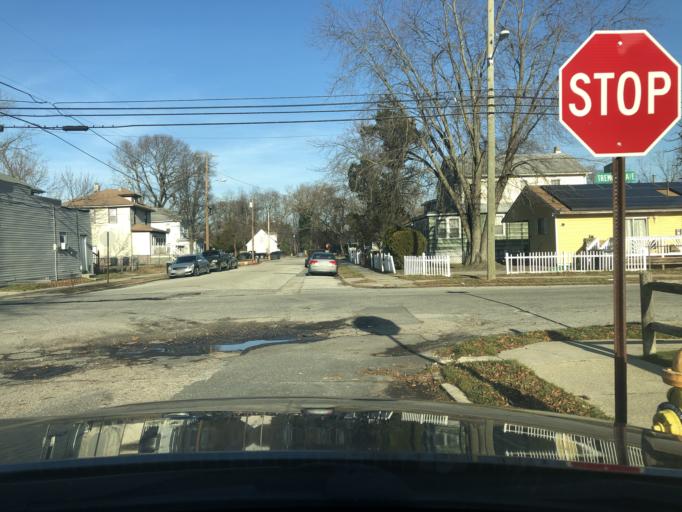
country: US
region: New Jersey
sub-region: Atlantic County
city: Pleasantville
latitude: 39.3850
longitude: -74.5389
